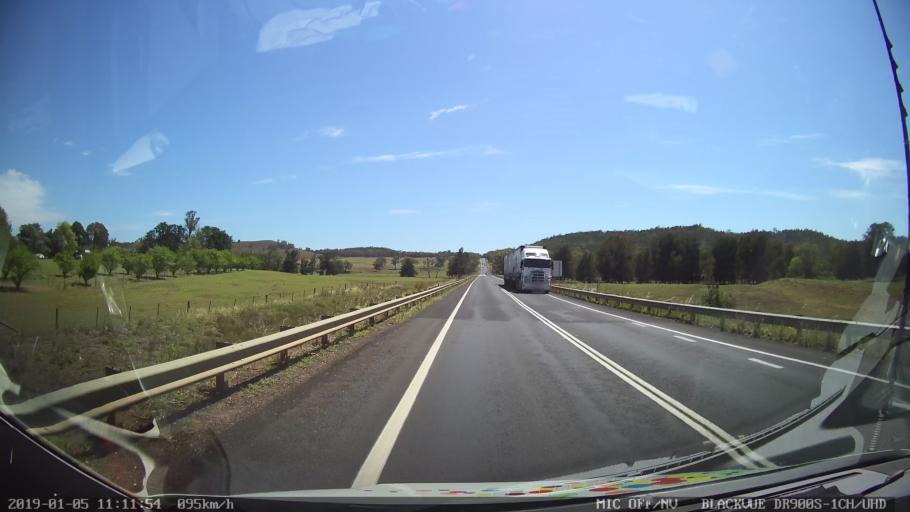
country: AU
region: New South Wales
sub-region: Warrumbungle Shire
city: Coonabarabran
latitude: -31.3876
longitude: 149.2547
